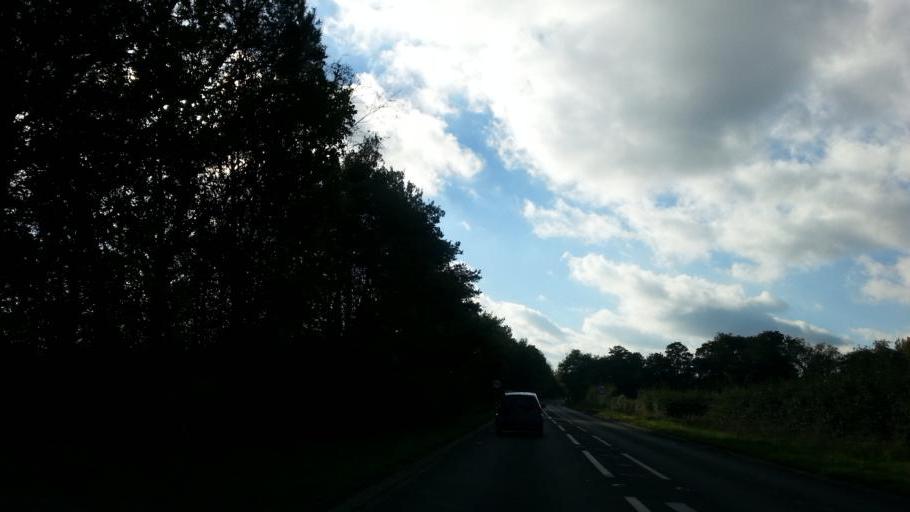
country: GB
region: England
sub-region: Norfolk
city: Ditchingham
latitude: 52.4838
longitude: 1.4898
